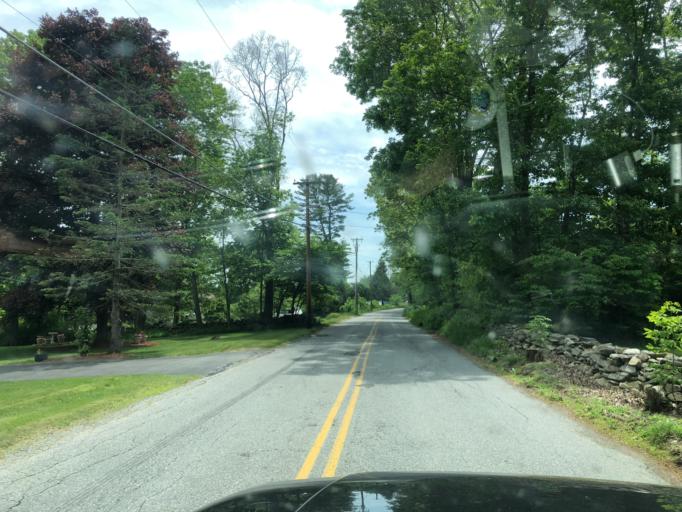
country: US
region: Connecticut
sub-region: Windham County
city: Thompson
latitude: 41.9710
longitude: -71.8368
